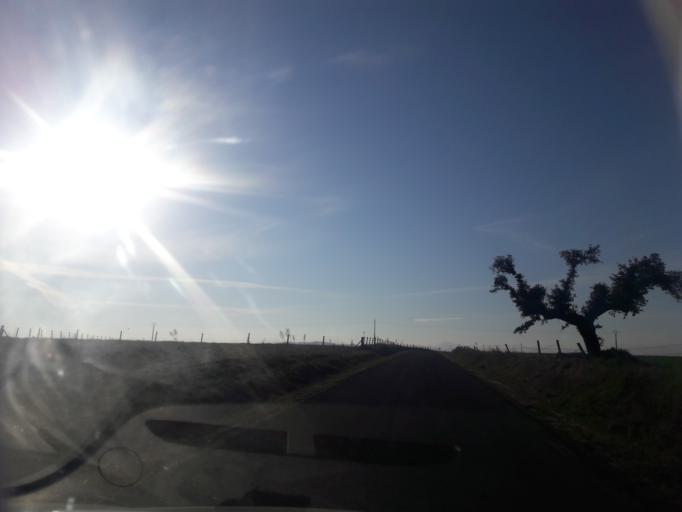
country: ES
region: Castille and Leon
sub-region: Provincia de Salamanca
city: Salvatierra de Tormes
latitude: 40.6129
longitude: -5.6050
